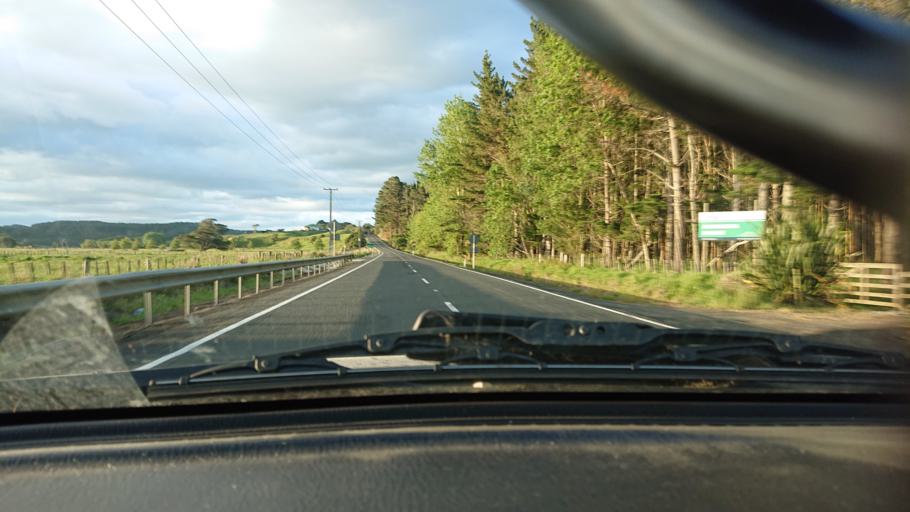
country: NZ
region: Auckland
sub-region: Auckland
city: Parakai
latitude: -36.5058
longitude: 174.4565
